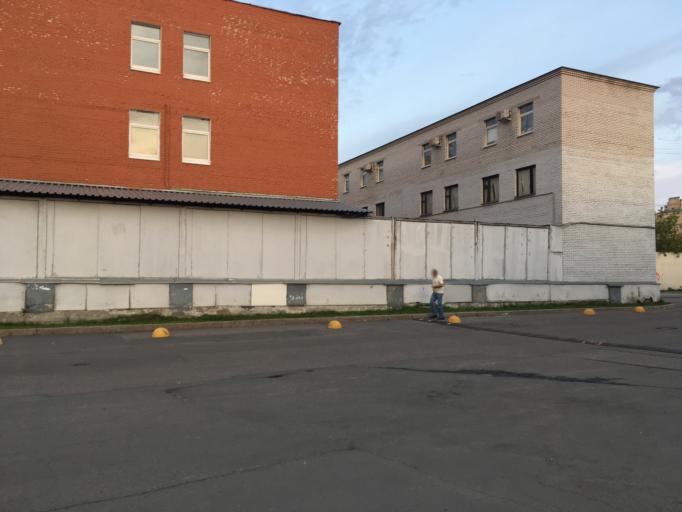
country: RU
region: St.-Petersburg
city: Centralniy
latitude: 59.9147
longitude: 30.3421
